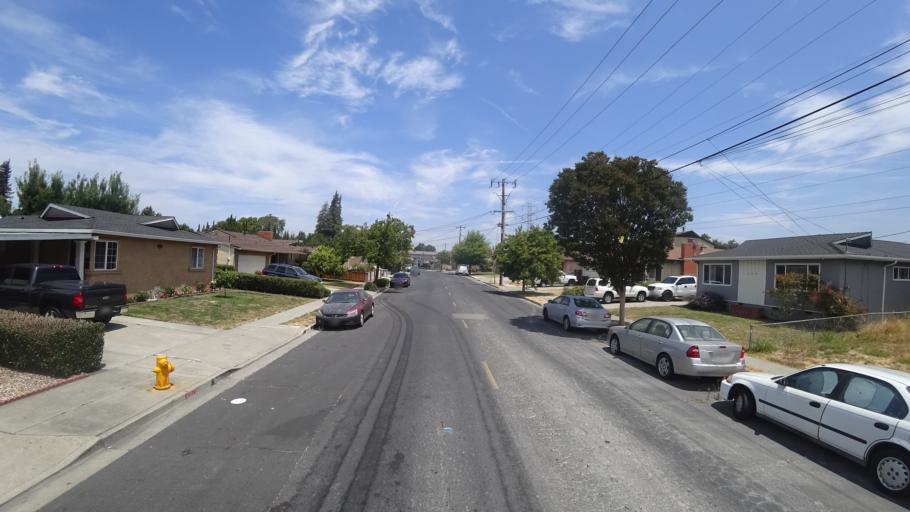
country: US
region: California
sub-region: Alameda County
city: Hayward
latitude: 37.6464
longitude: -122.0876
